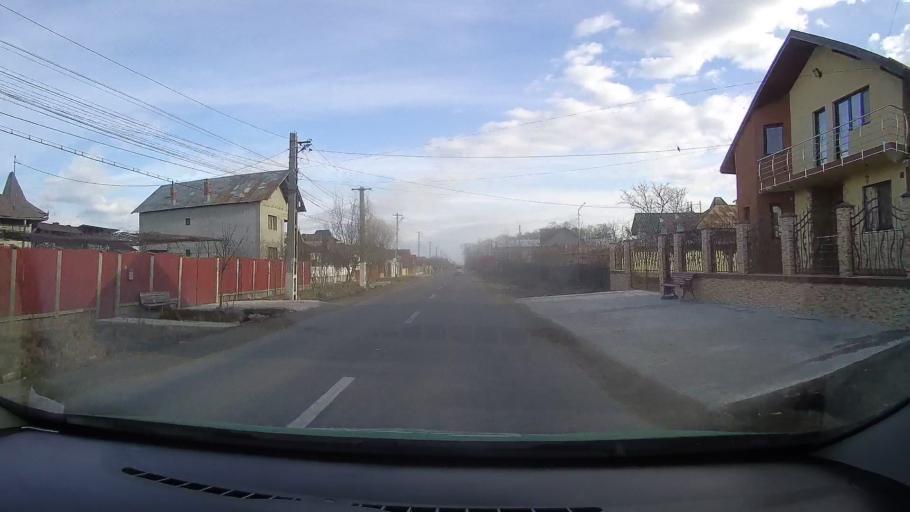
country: RO
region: Dambovita
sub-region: Comuna Vacaresti
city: Vacaresti
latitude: 44.8609
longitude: 25.4799
